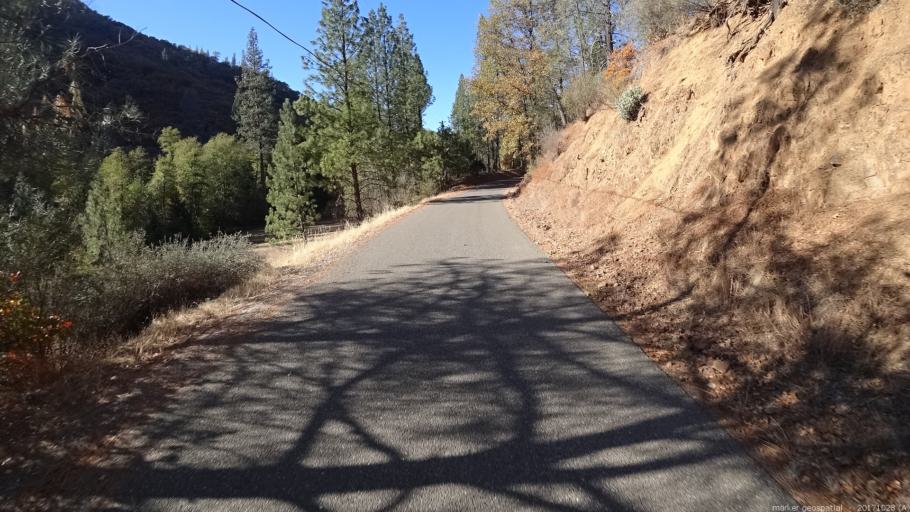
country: US
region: California
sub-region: Shasta County
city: Shasta
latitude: 40.7591
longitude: -122.6061
